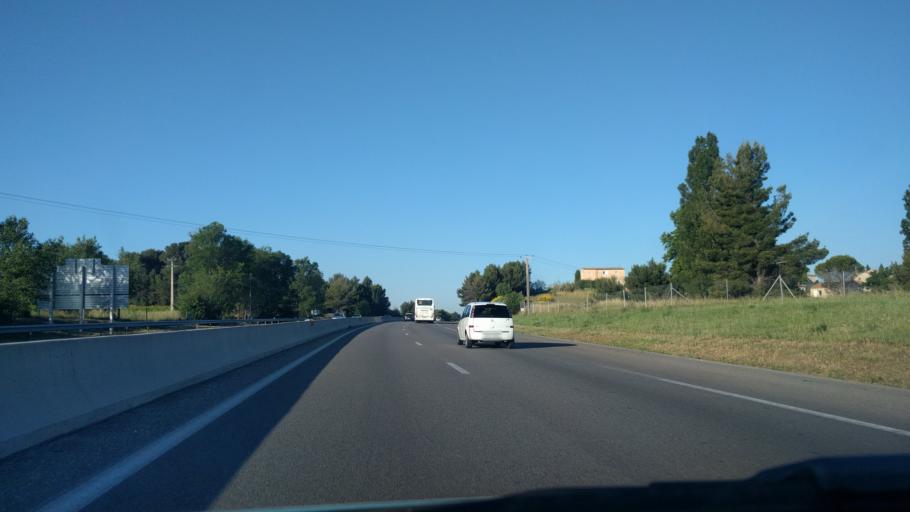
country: FR
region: Provence-Alpes-Cote d'Azur
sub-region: Departement des Bouches-du-Rhone
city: Venelles
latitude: 43.5779
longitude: 5.4741
